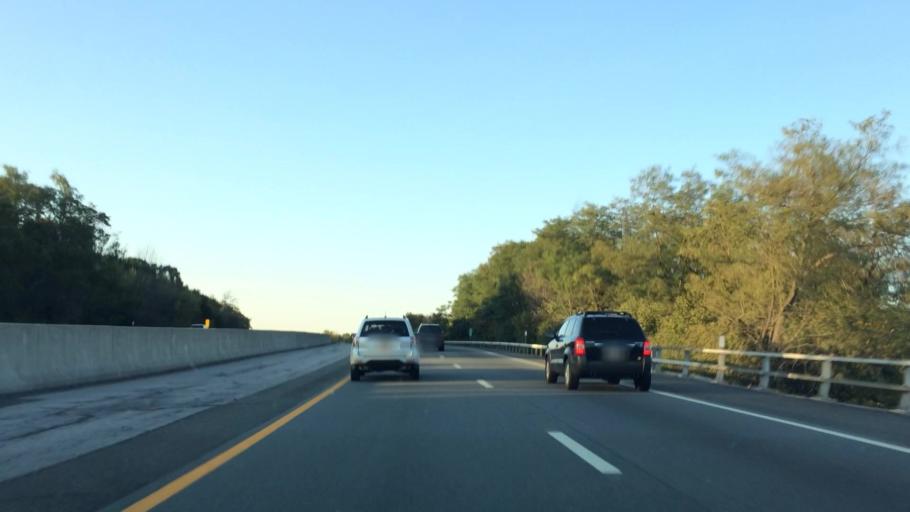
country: US
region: New York
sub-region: Orange County
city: Vails Gate
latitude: 41.4521
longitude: -74.0643
